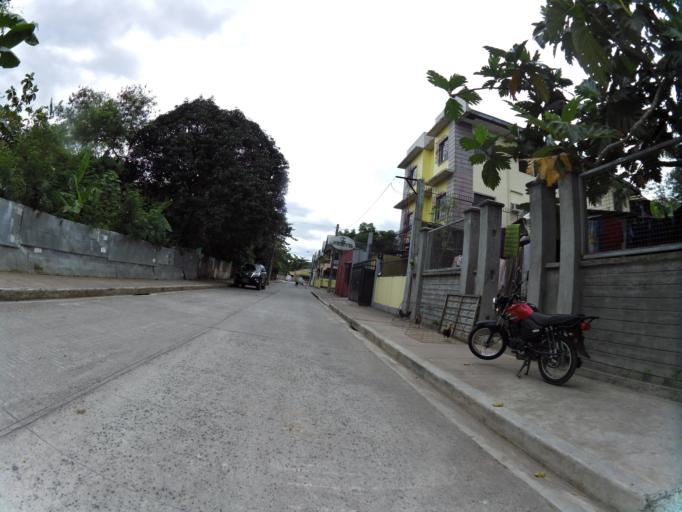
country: PH
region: Calabarzon
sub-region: Province of Rizal
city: Antipolo
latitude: 14.6379
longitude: 121.1102
